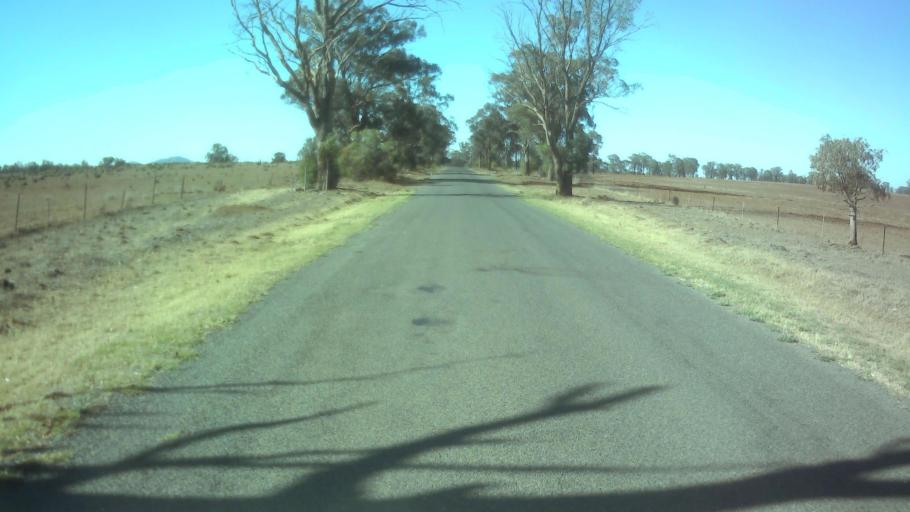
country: AU
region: New South Wales
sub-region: Forbes
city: Forbes
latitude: -33.7002
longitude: 147.8068
